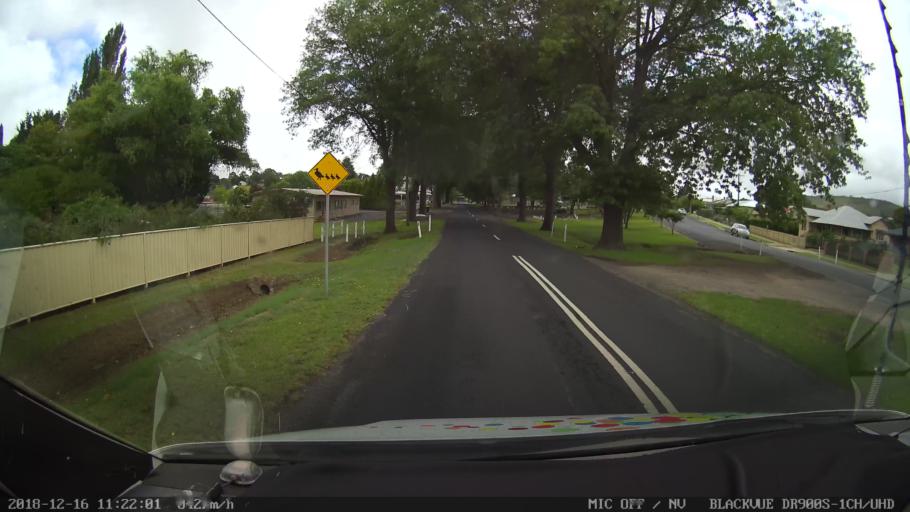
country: AU
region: New South Wales
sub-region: Tenterfield Municipality
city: Carrolls Creek
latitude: -29.0539
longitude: 152.0230
